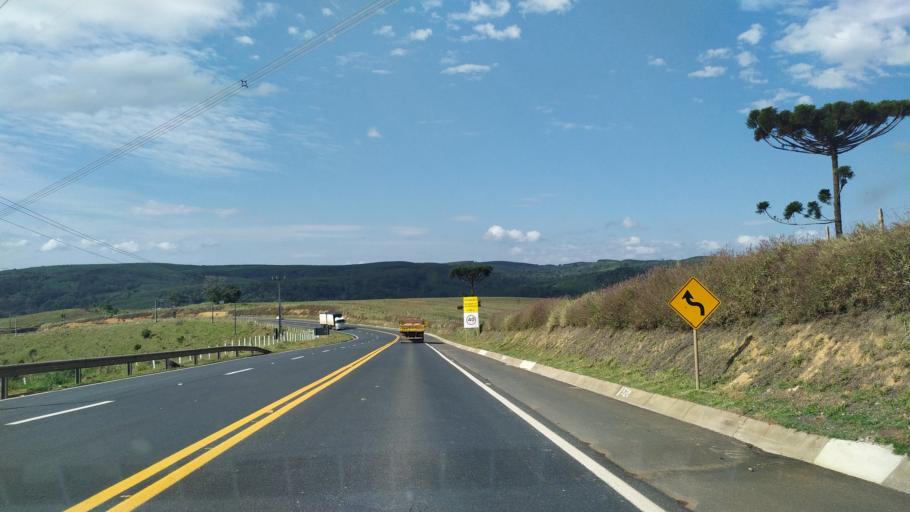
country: BR
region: Parana
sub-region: Telemaco Borba
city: Telemaco Borba
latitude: -24.2849
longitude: -50.7105
